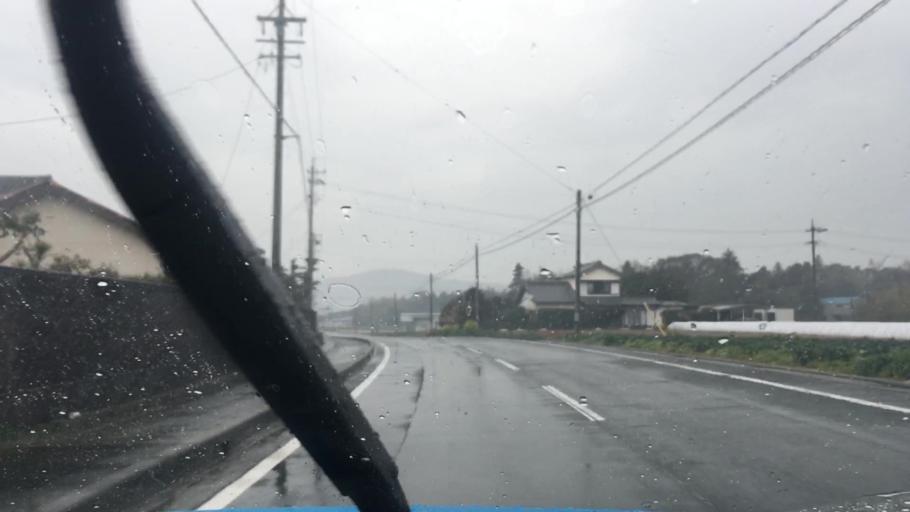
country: JP
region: Aichi
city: Tahara
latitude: 34.6548
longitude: 137.2889
